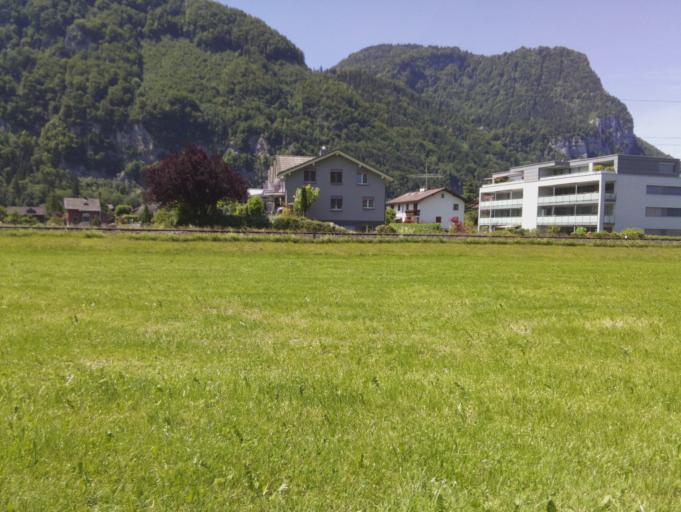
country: CH
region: Glarus
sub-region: Glarus
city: Nafels
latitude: 47.0890
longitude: 9.0638
